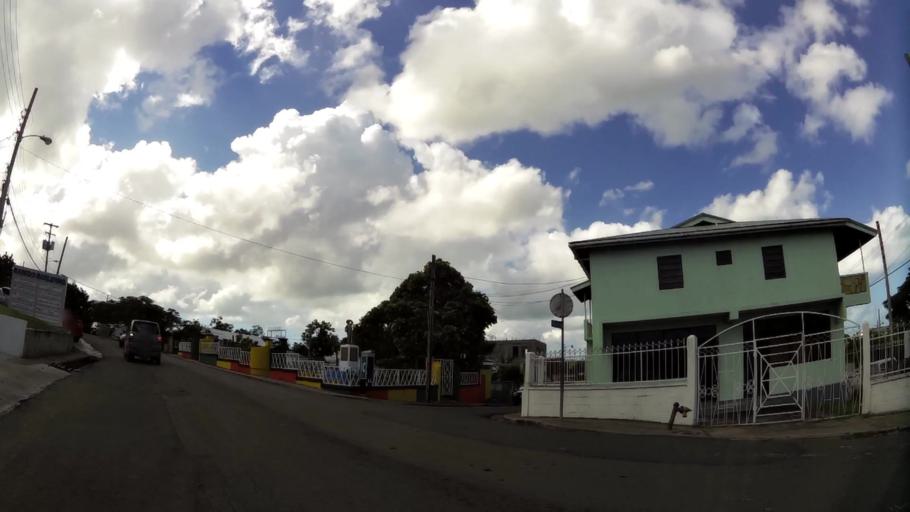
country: AG
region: Saint John
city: Saint John's
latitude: 17.1179
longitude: -61.8399
